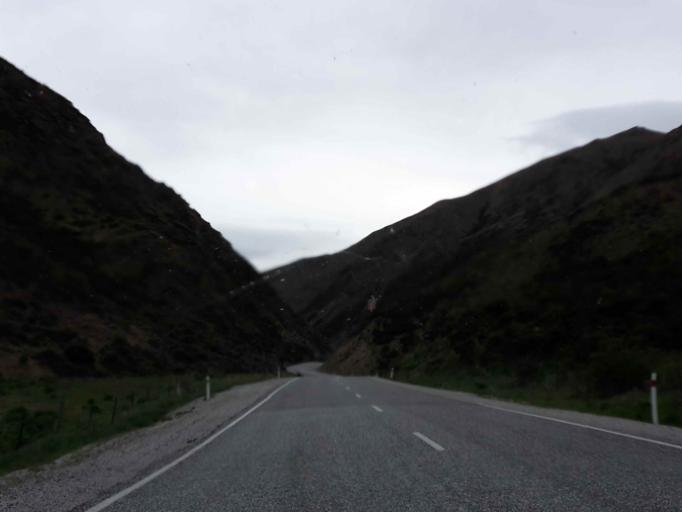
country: NZ
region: Otago
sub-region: Queenstown-Lakes District
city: Wanaka
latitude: -44.5999
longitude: 169.5577
